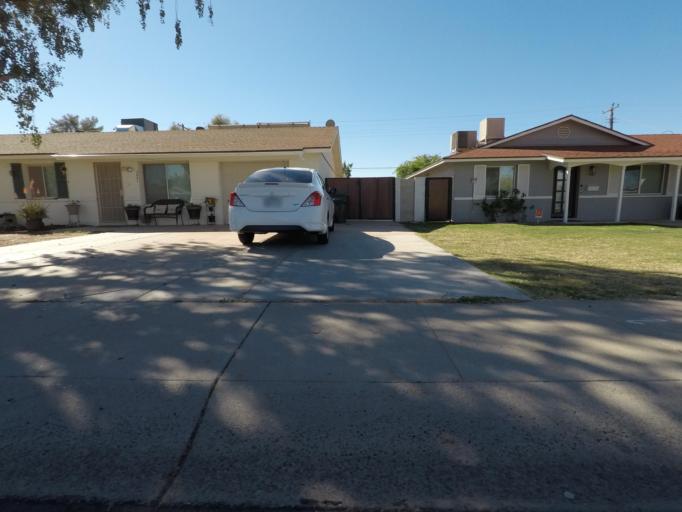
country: US
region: Arizona
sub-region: Maricopa County
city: Glendale
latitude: 33.5465
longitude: -112.1409
